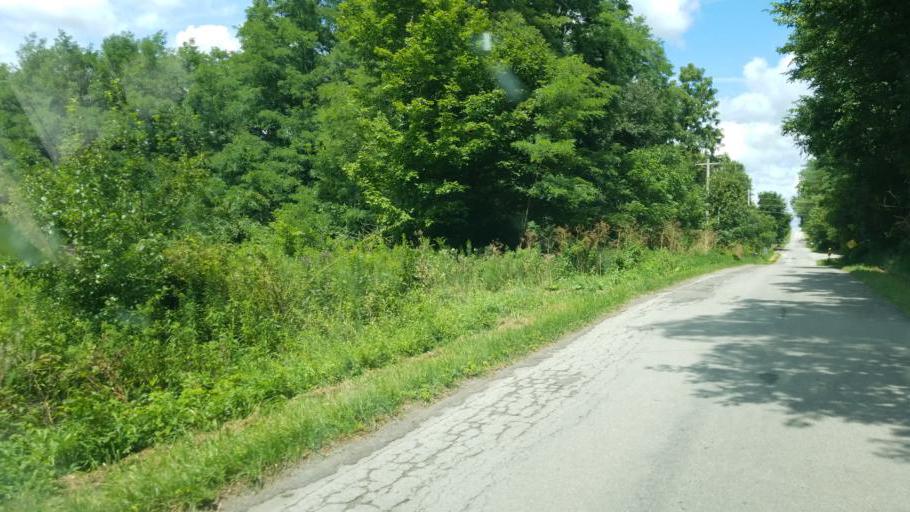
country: US
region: Ohio
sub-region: Knox County
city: Centerburg
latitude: 40.3742
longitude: -82.7239
